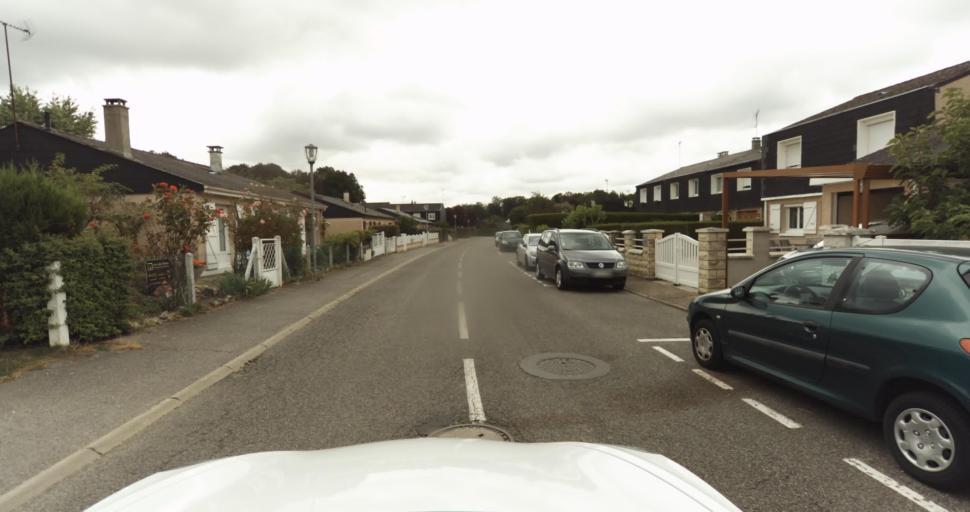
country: FR
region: Haute-Normandie
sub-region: Departement de l'Eure
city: Saint-Sebastien-de-Morsent
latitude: 49.0049
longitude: 1.0864
